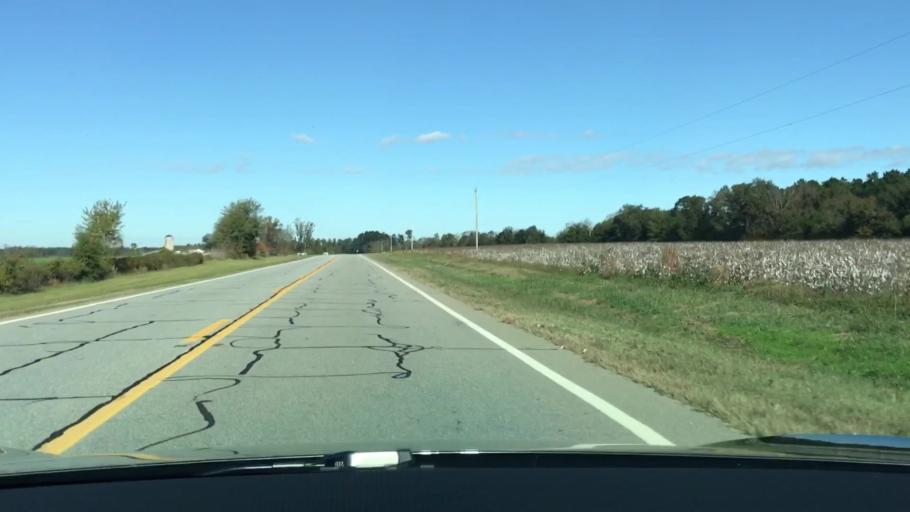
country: US
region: Georgia
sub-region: Warren County
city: Warrenton
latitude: 33.3651
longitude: -82.5987
